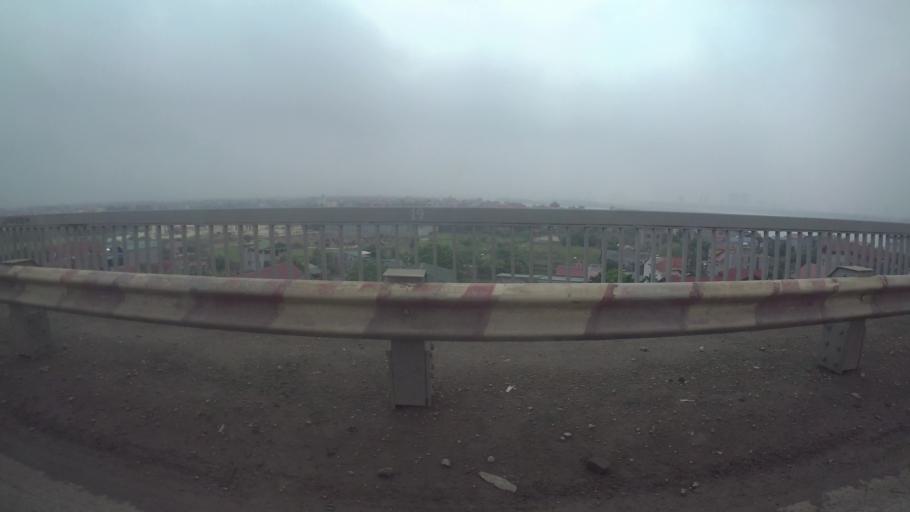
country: VN
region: Ha Noi
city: Tay Ho
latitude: 21.1041
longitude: 105.7870
